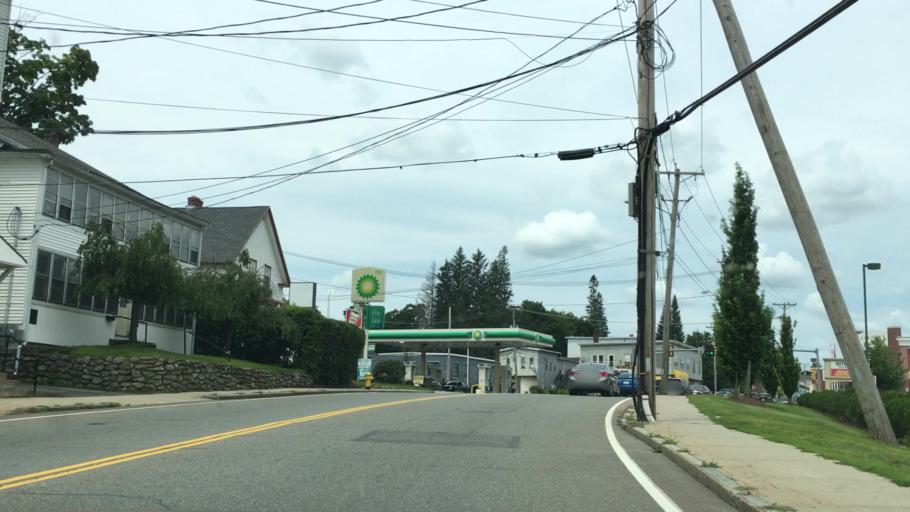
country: US
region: Massachusetts
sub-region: Worcester County
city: Gardner
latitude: 42.5709
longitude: -71.9939
